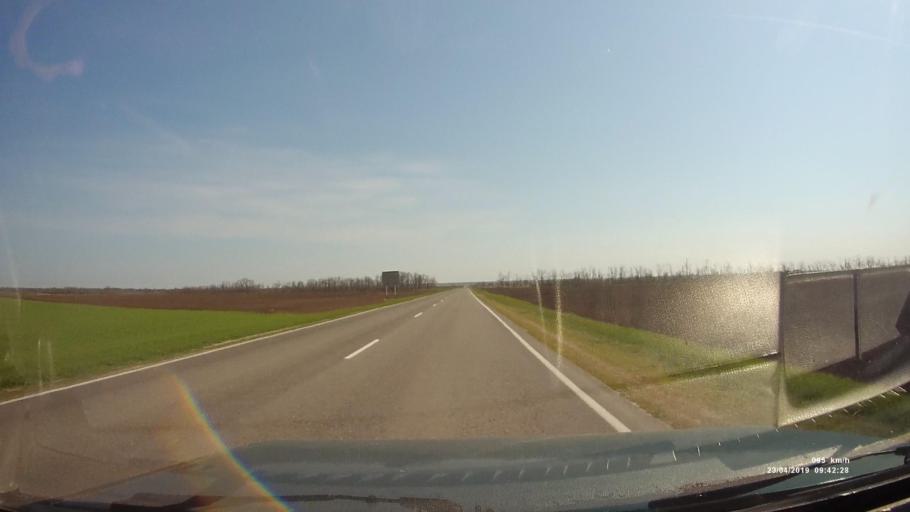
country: RU
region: Rostov
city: Orlovskiy
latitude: 46.8702
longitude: 41.9797
